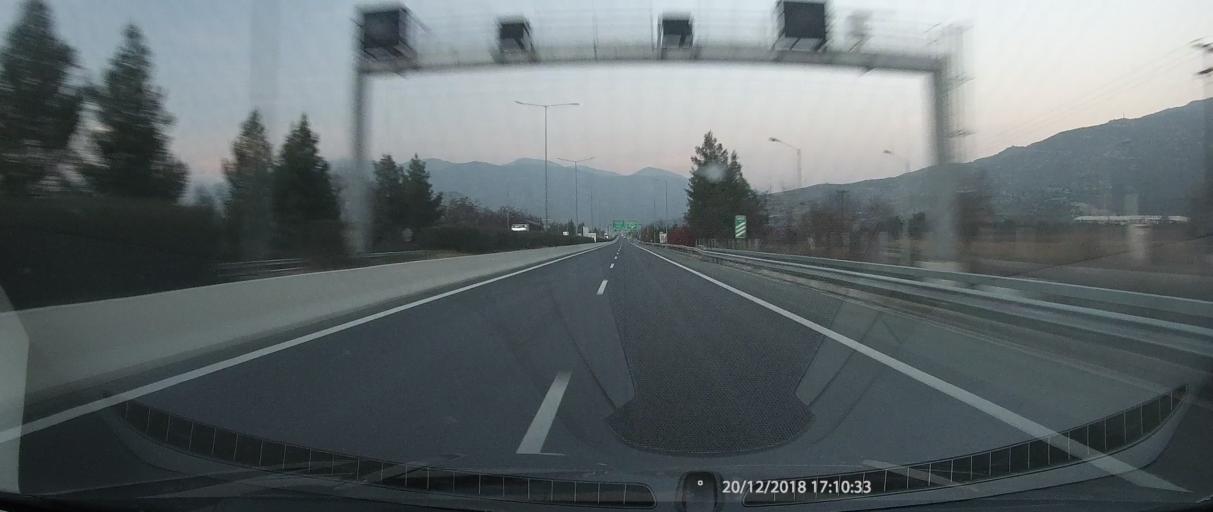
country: GR
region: Thessaly
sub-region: Nomos Larisis
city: Makrychori
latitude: 39.8218
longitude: 22.5102
